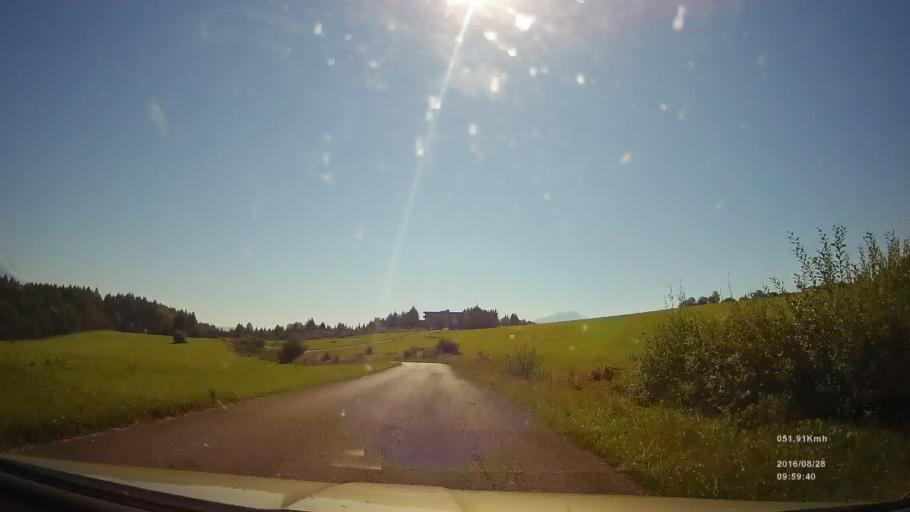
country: SK
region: Zilinsky
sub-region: Okres Liptovsky Mikulas
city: Liptovsky Mikulas
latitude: 49.1119
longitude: 19.4869
